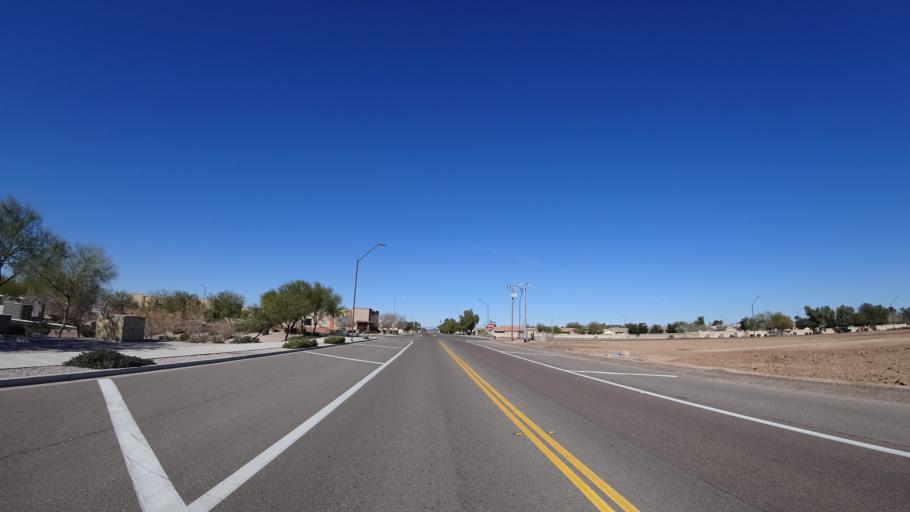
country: US
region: Arizona
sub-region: Maricopa County
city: Goodyear
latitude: 33.4201
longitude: -112.3579
